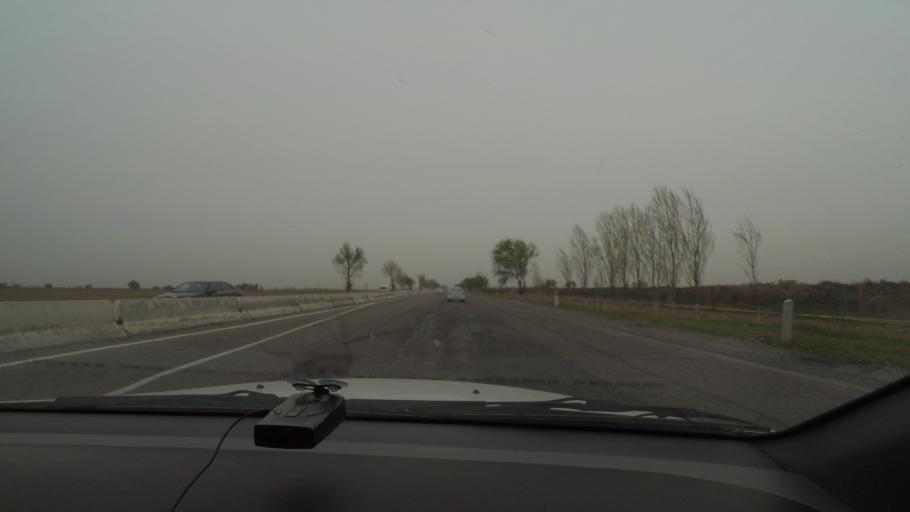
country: UZ
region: Jizzax
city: Gagarin
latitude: 40.5239
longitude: 68.3352
